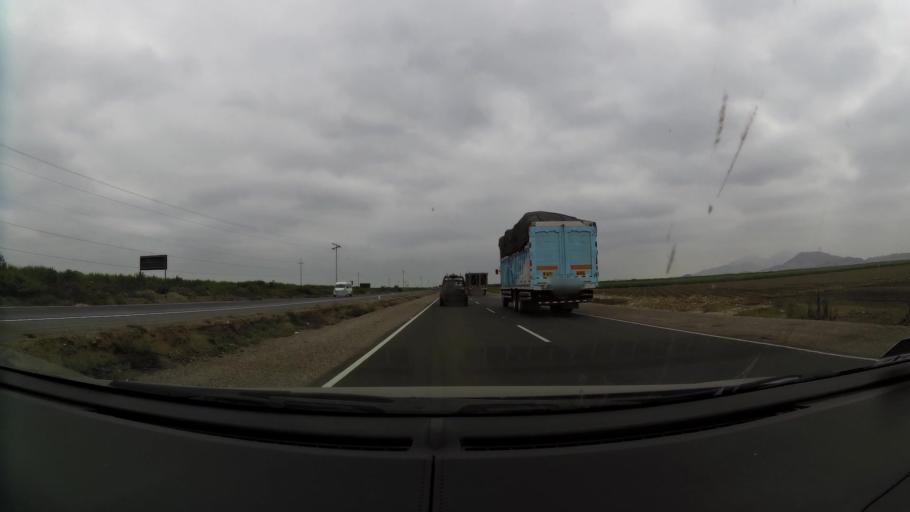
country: PE
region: La Libertad
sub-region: Ascope
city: Chocope
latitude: -7.7887
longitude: -79.2336
